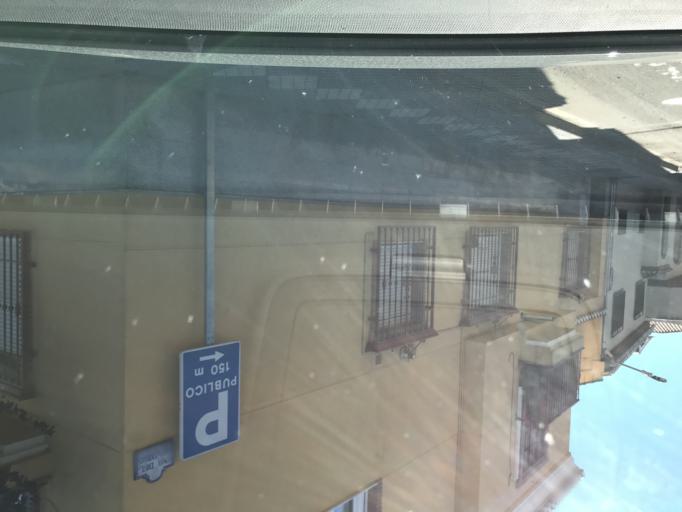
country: ES
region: Andalusia
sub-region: Provincia de Granada
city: Maracena
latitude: 37.2100
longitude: -3.6416
